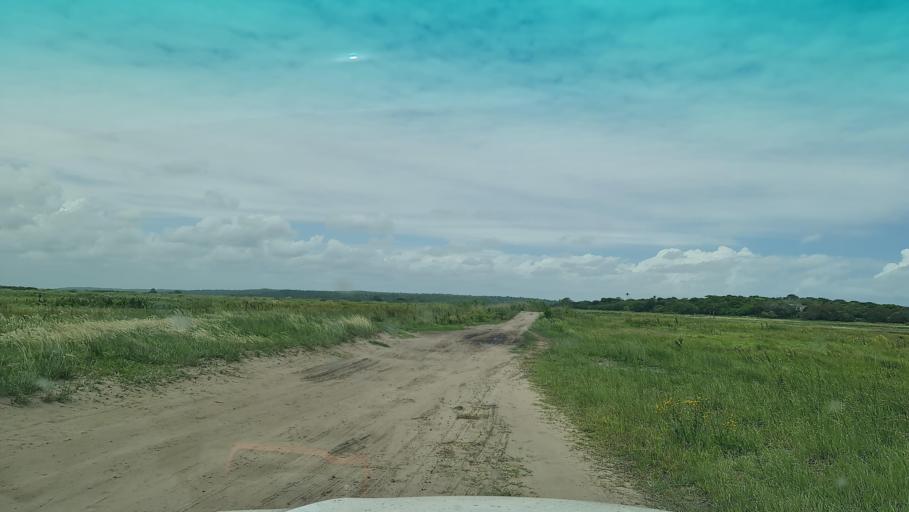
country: MZ
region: Maputo
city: Manhica
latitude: -25.5253
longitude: 32.8560
